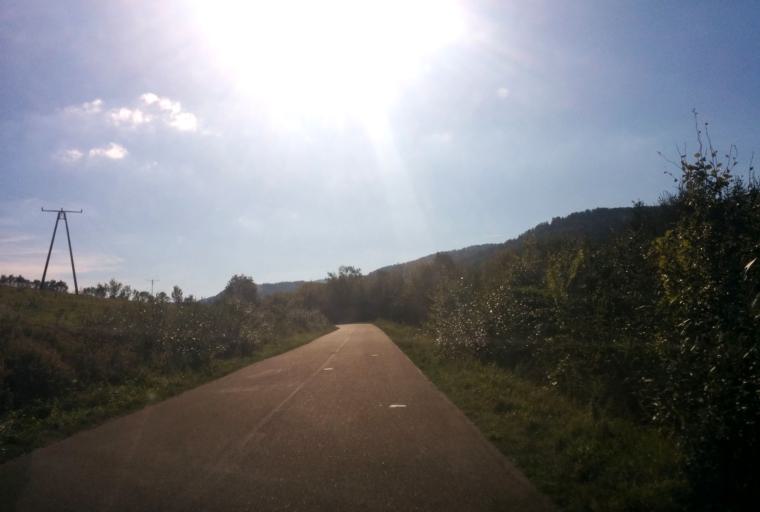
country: PL
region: Subcarpathian Voivodeship
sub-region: Powiat leski
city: Polanczyk
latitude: 49.2932
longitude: 22.4230
